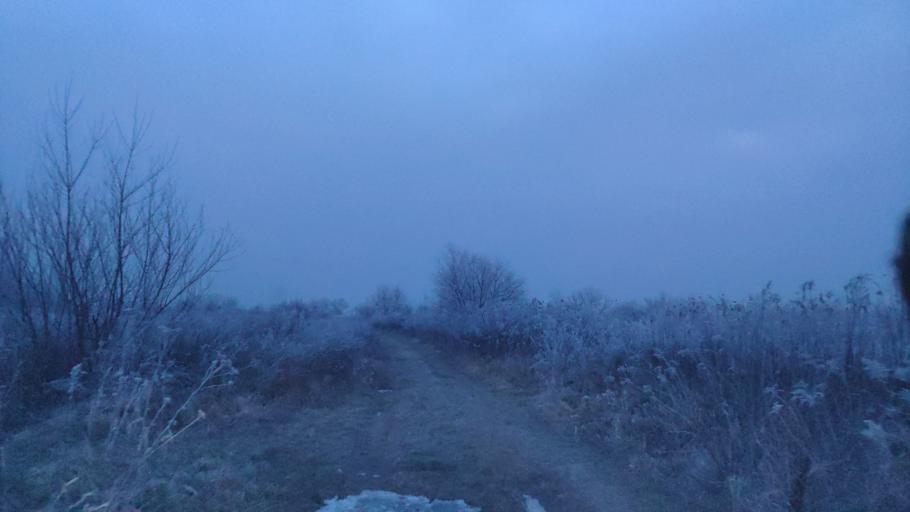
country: SK
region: Kosicky
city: Kosice
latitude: 48.6148
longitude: 21.3352
